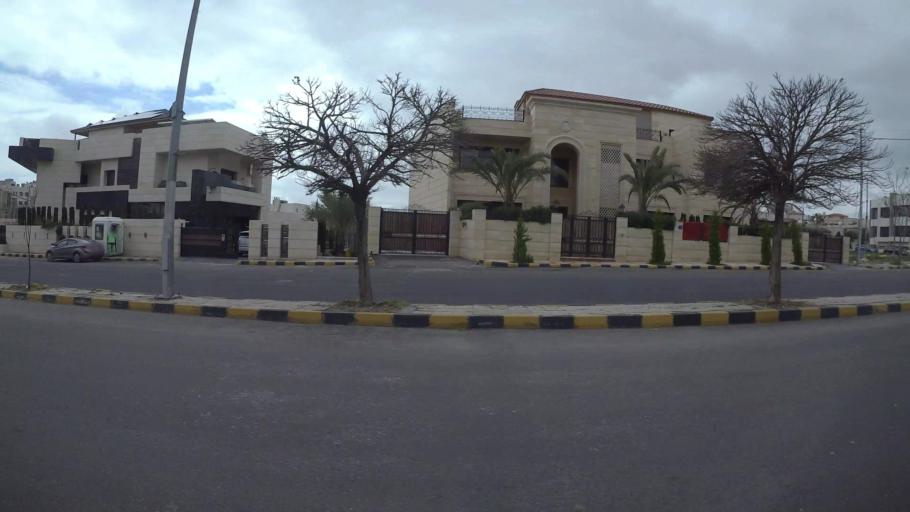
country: JO
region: Amman
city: Wadi as Sir
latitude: 31.9893
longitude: 35.8364
